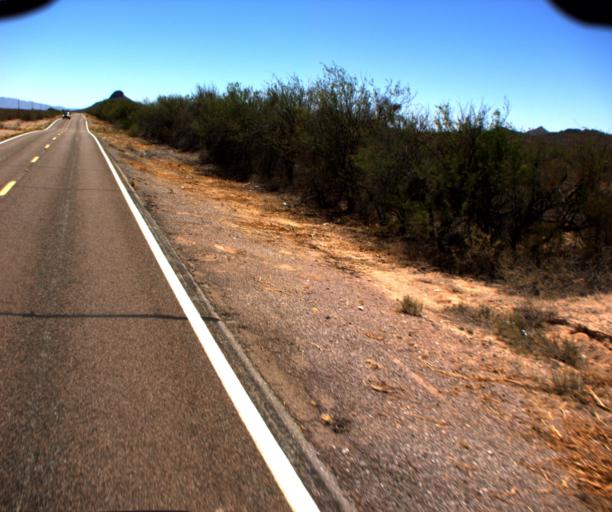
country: US
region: Arizona
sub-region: Pima County
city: Ajo
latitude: 32.2057
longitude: -112.5646
